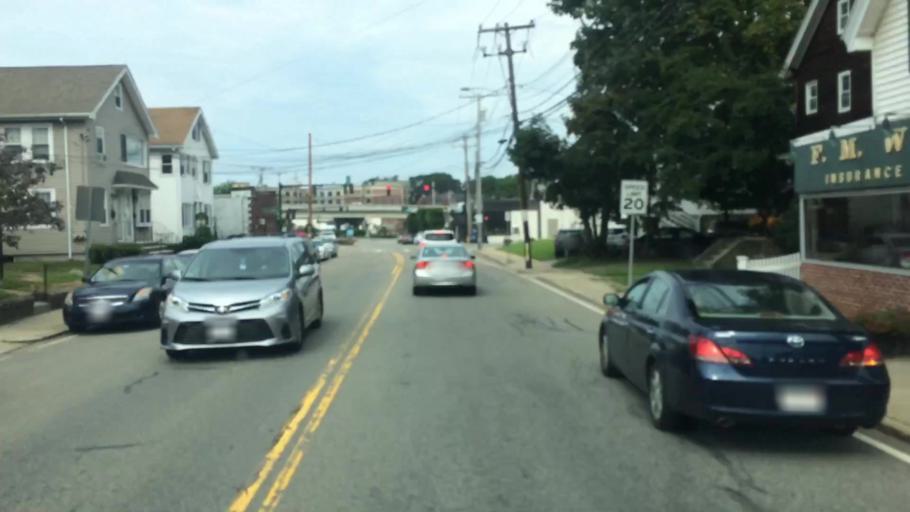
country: US
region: Massachusetts
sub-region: Norfolk County
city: Dedham
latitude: 42.2487
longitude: -71.1686
